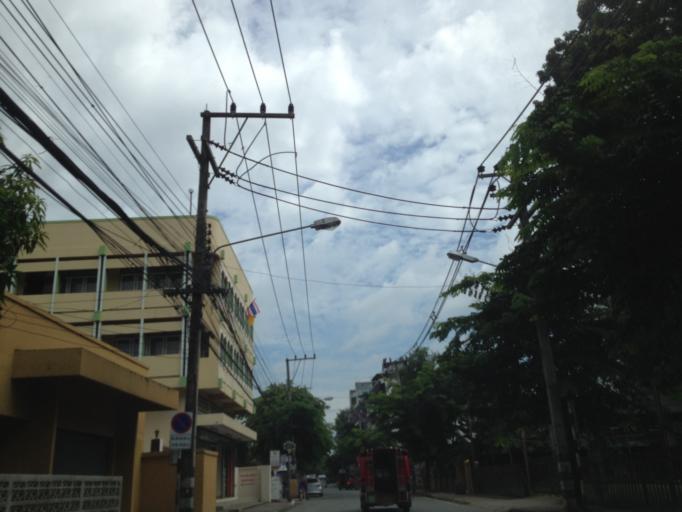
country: TH
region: Chiang Mai
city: Chiang Mai
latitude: 18.7830
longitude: 99.0031
